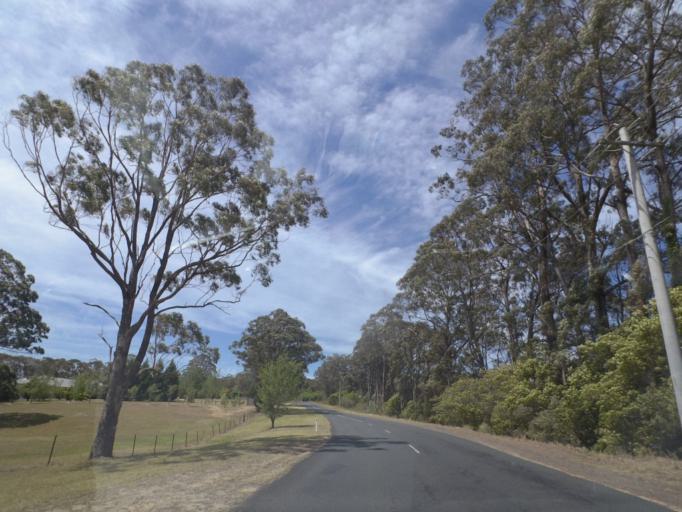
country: AU
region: New South Wales
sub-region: Wingecarribee
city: Colo Vale
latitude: -34.4075
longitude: 150.5279
